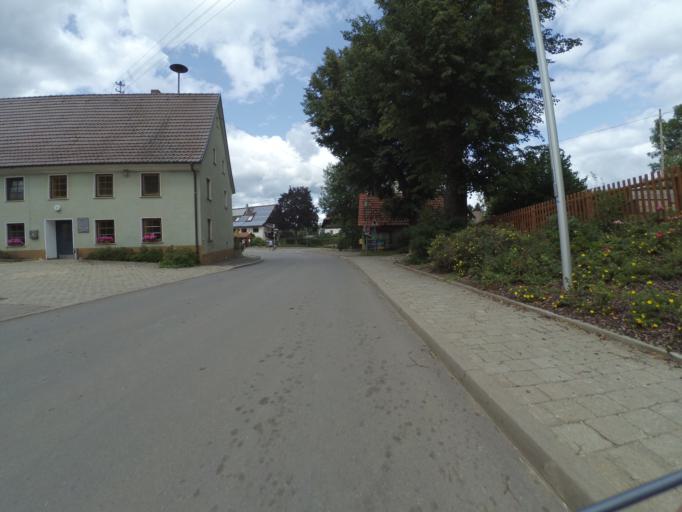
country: DE
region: Baden-Wuerttemberg
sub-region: Freiburg Region
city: Hufingen
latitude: 47.9085
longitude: 8.5389
